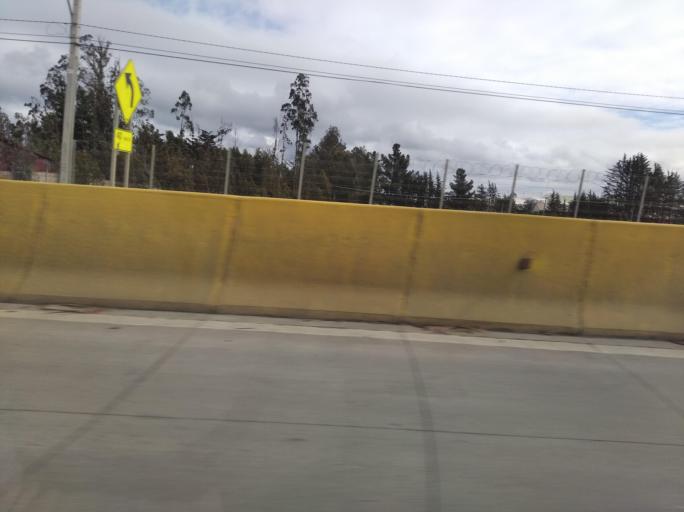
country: CL
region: Valparaiso
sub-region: Provincia de Valparaiso
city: Valparaiso
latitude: -33.0981
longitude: -71.5812
